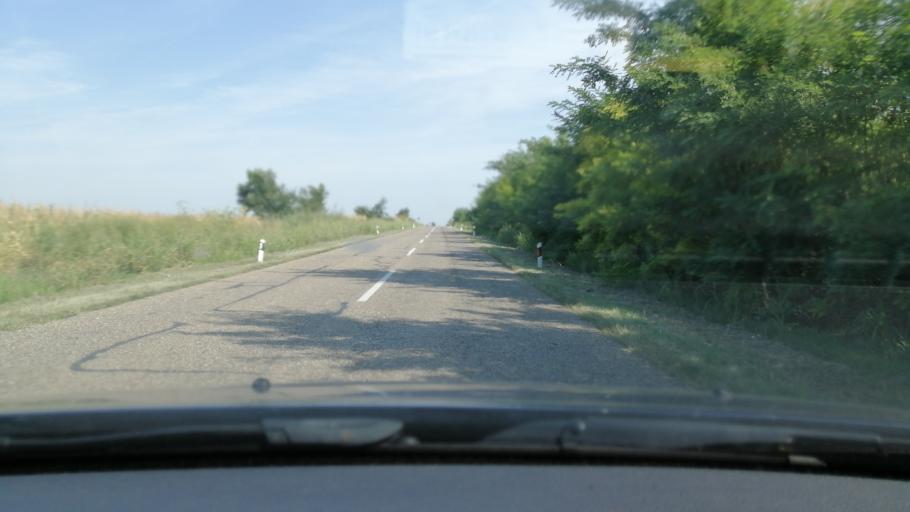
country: RS
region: Autonomna Pokrajina Vojvodina
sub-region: Juznobanatski Okrug
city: Kovacica
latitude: 45.1523
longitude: 20.6168
